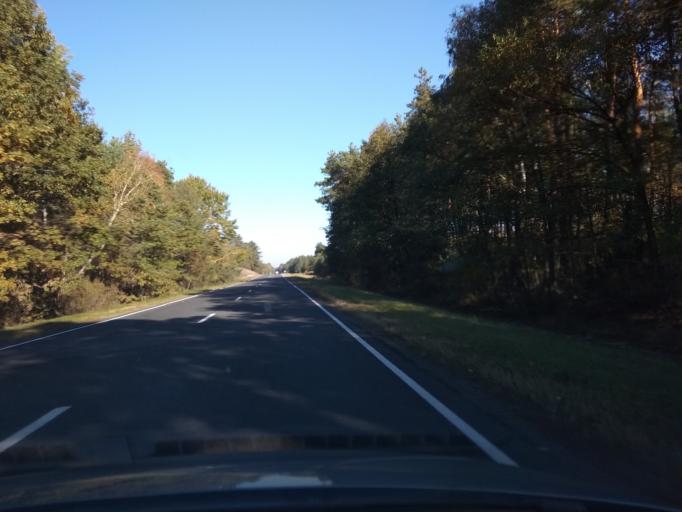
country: BY
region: Brest
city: Kobryn
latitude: 52.0488
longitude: 24.2770
